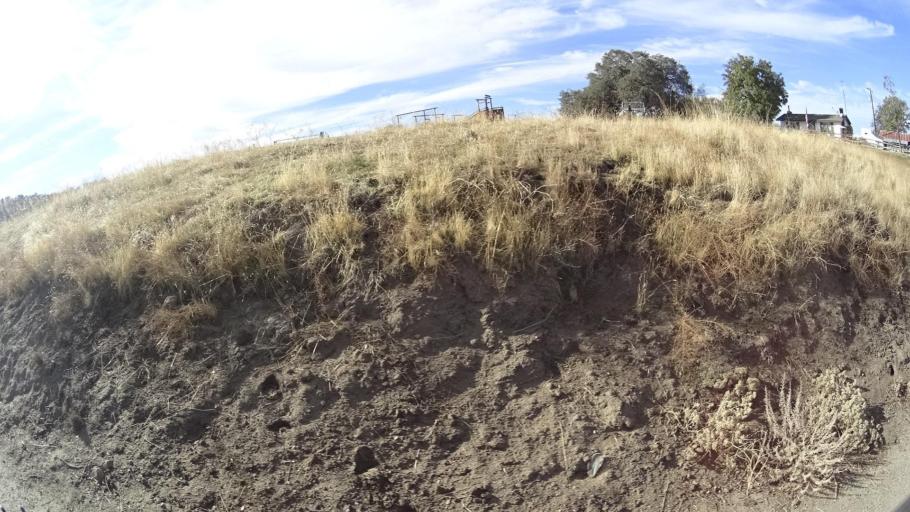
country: US
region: California
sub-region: Kern County
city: Oildale
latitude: 35.5799
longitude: -118.8128
